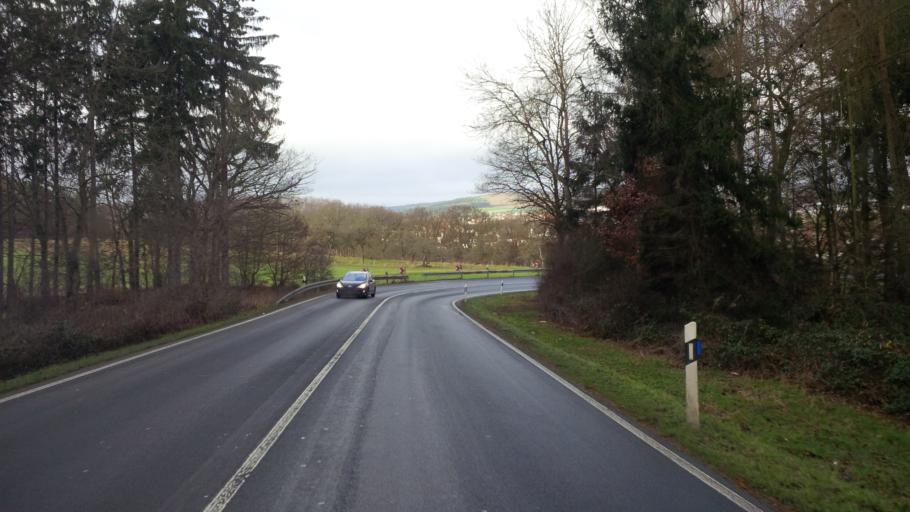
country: DE
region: Hesse
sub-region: Regierungsbezirk Darmstadt
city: Usingen
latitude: 50.3242
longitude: 8.5466
